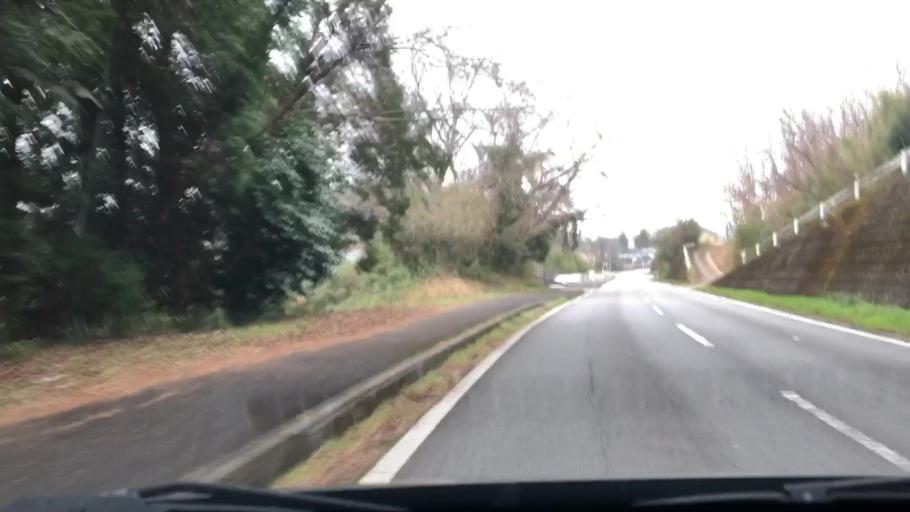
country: JP
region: Oita
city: Usuki
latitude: 33.0164
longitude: 131.6677
